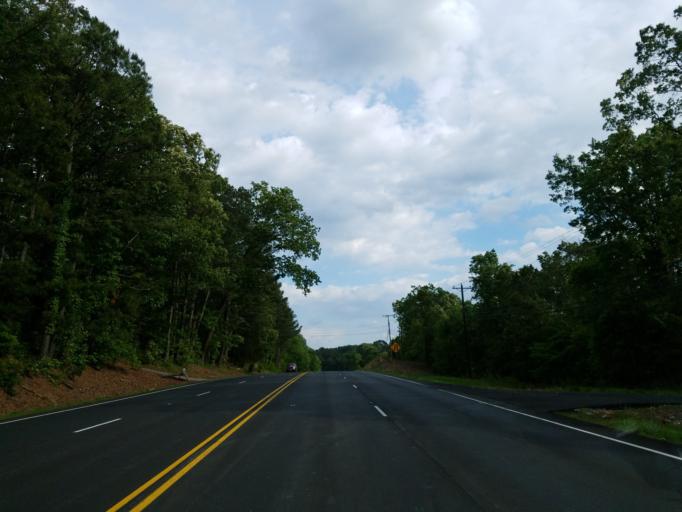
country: US
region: Georgia
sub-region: Pickens County
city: Nelson
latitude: 34.4179
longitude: -84.3917
